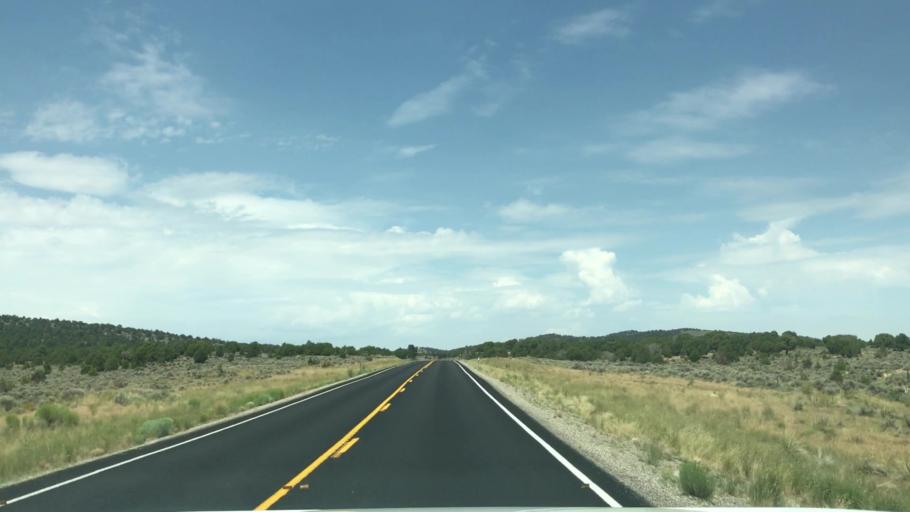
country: US
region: Nevada
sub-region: Eureka County
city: Eureka
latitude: 39.3901
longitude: -115.4519
